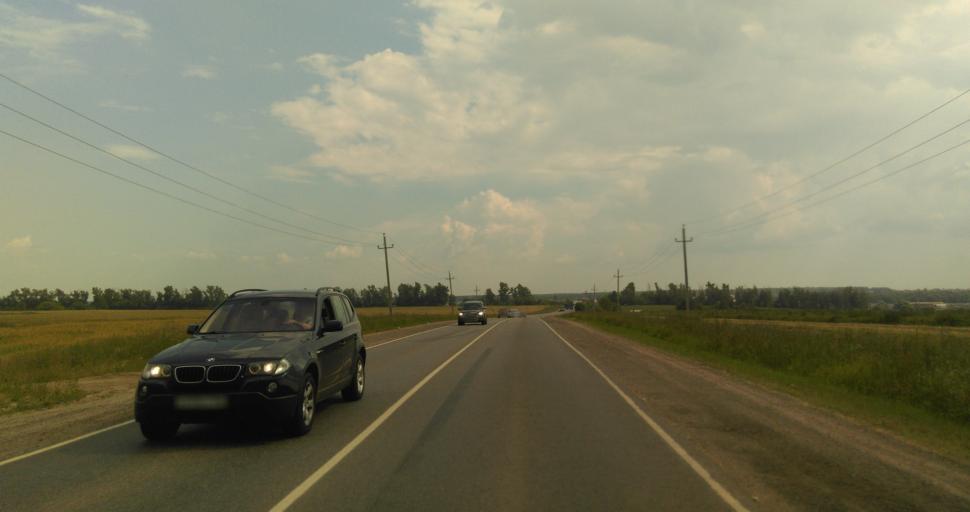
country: RU
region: Moskovskaya
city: Zhitnevo
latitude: 55.3607
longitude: 37.9056
